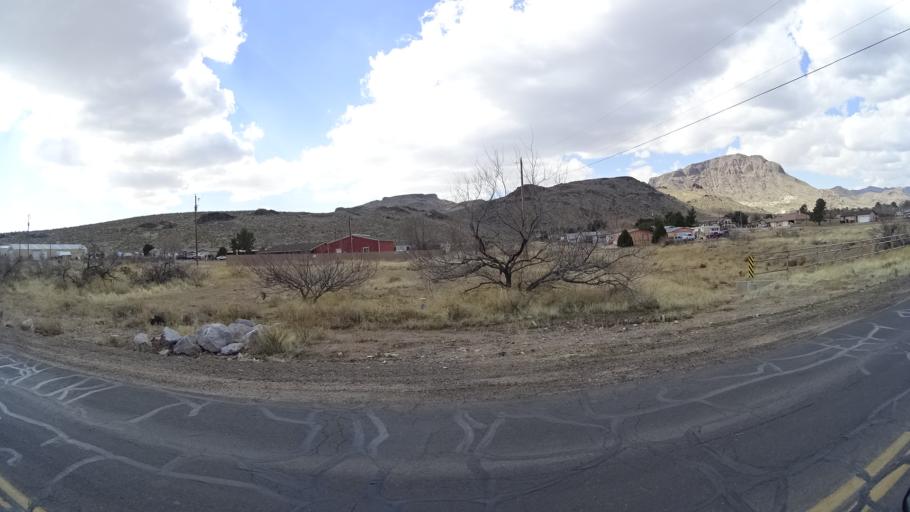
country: US
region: Arizona
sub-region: Mohave County
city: New Kingman-Butler
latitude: 35.2586
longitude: -114.0383
